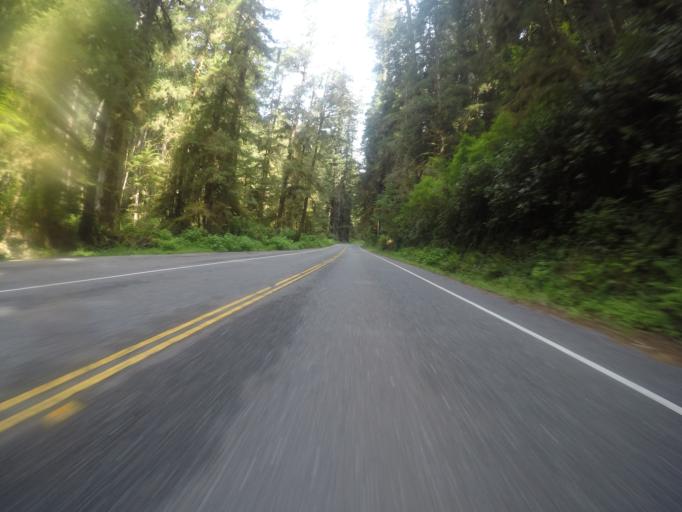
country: US
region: California
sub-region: Del Norte County
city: Bertsch-Oceanview
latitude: 41.4345
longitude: -124.0389
